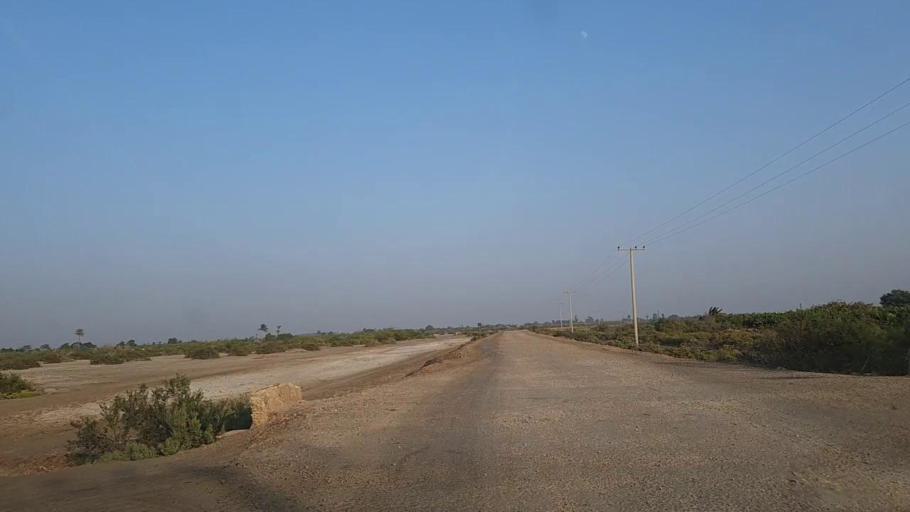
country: PK
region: Sindh
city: Keti Bandar
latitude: 24.2792
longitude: 67.6392
